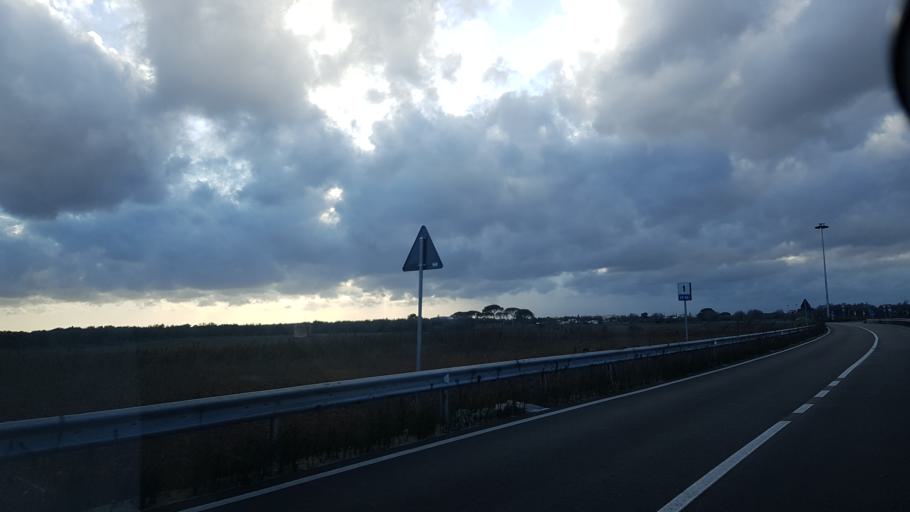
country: IT
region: Apulia
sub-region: Provincia di Brindisi
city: San Pietro Vernotico
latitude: 40.4873
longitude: 18.0230
